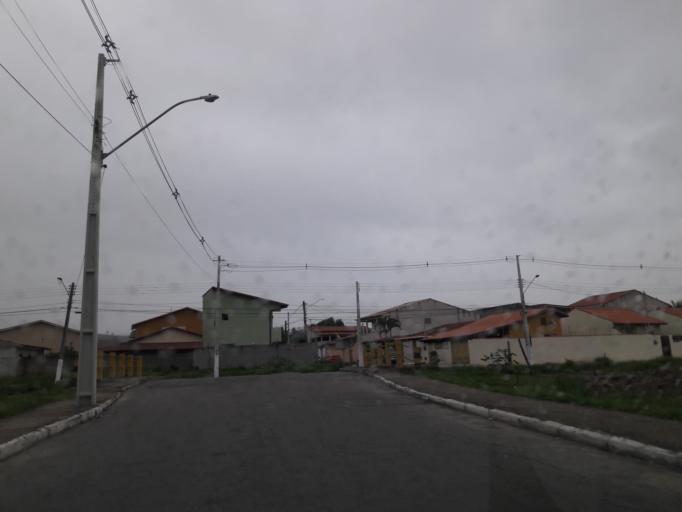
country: BR
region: Rio de Janeiro
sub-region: Resende
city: Resende
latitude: -22.4852
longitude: -44.4986
